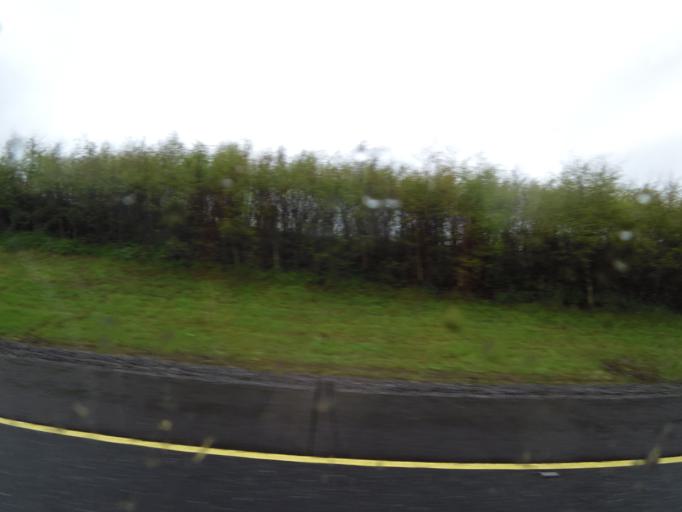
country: IE
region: Leinster
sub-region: Kildare
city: Maynooth
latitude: 53.3670
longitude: -6.5915
